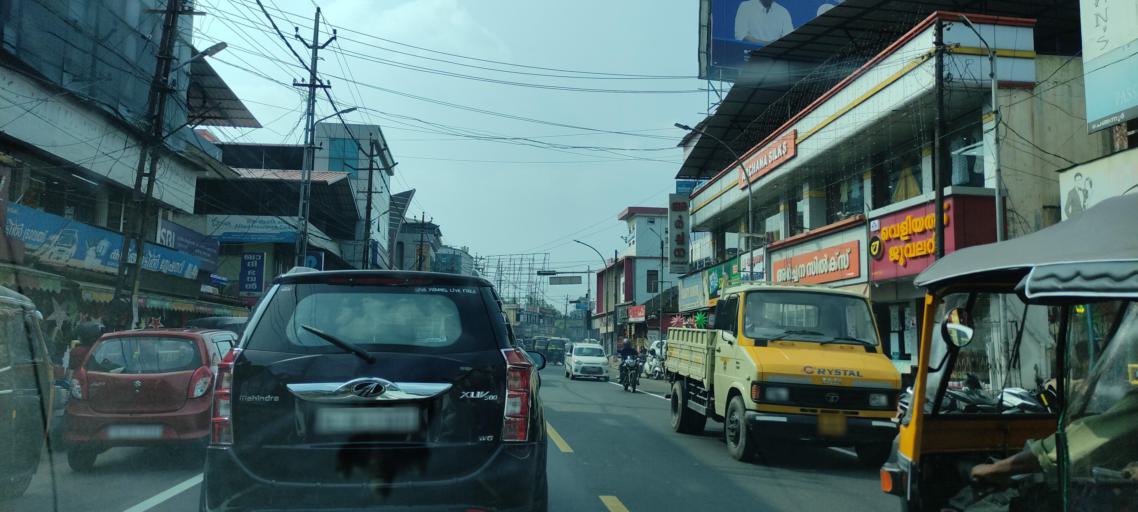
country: IN
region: Kerala
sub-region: Alappuzha
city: Chengannur
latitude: 9.3180
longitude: 76.6148
